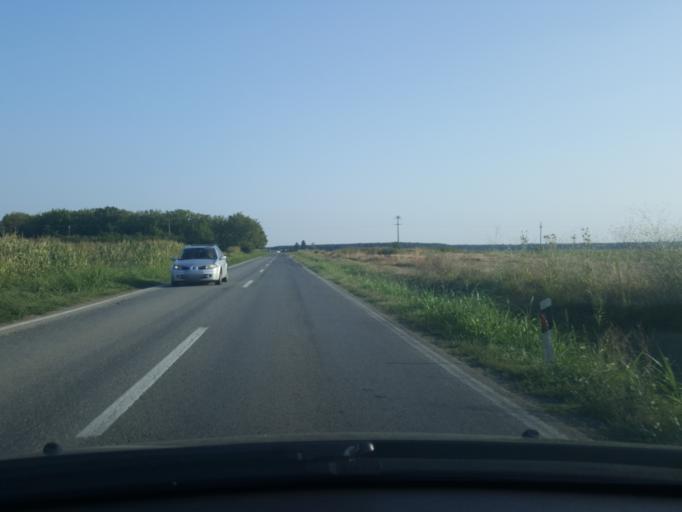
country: RS
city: Hrtkovci
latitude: 44.8578
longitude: 19.7714
